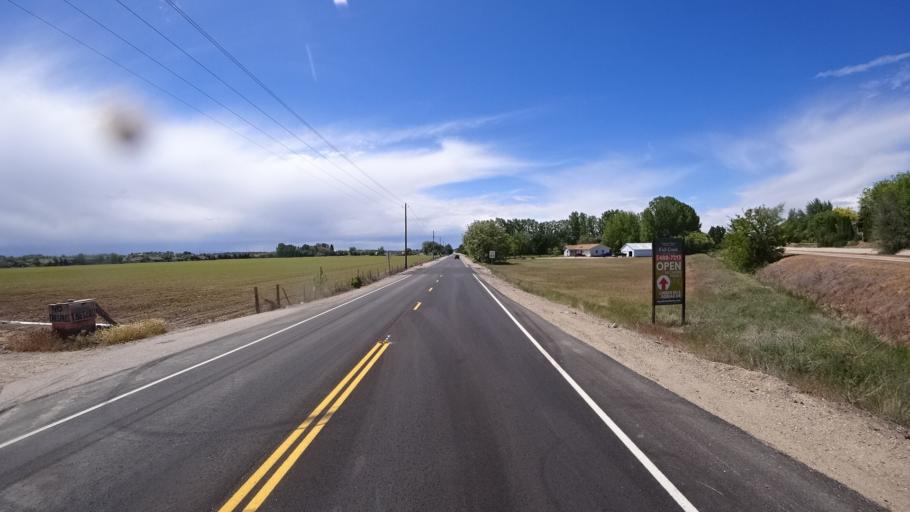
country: US
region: Idaho
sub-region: Ada County
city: Meridian
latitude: 43.5757
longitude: -116.3621
